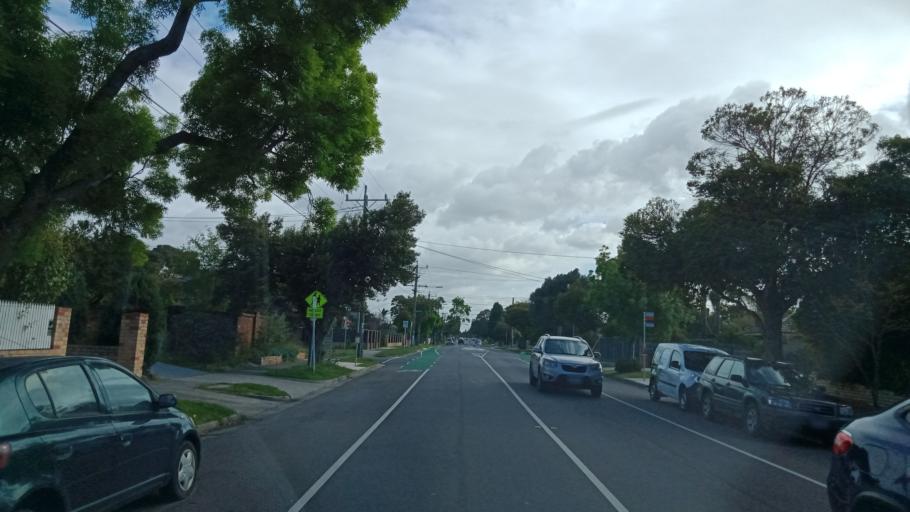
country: AU
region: Victoria
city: McKinnon
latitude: -37.9241
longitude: 145.0502
